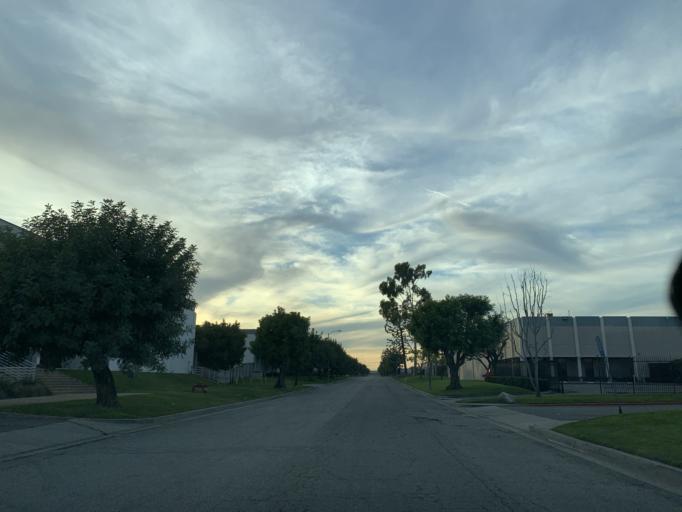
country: US
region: California
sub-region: Los Angeles County
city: Compton
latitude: 33.8789
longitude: -118.2296
